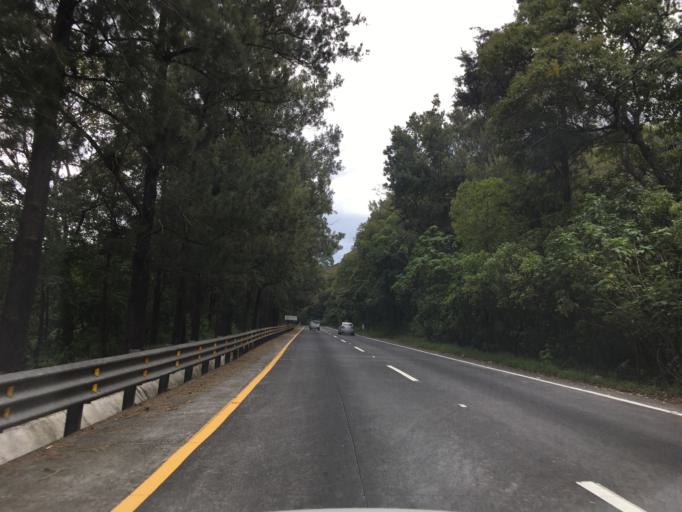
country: GT
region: Sacatepequez
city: Santa Lucia Milpas Altas
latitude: 14.5673
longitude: -90.6832
